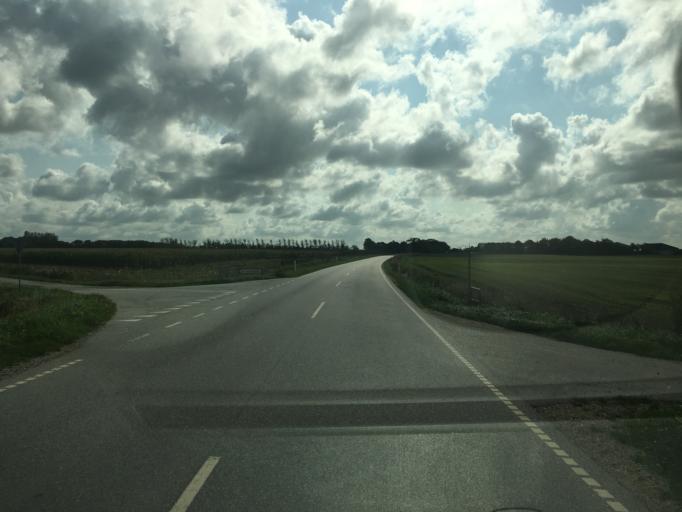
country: DK
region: South Denmark
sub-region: Tonder Kommune
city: Sherrebek
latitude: 55.1159
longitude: 8.8539
